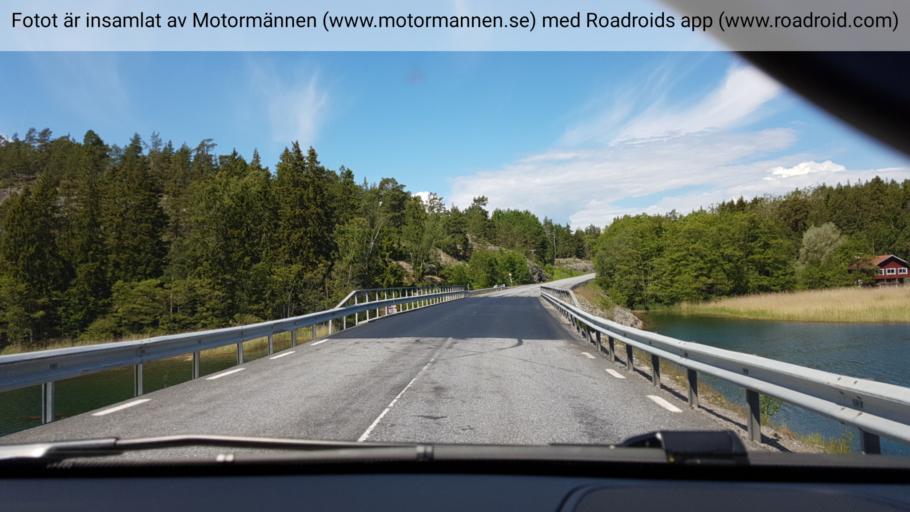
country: SE
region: Stockholm
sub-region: Nynashamns Kommun
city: Nynashamn
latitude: 58.9520
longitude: 18.0006
